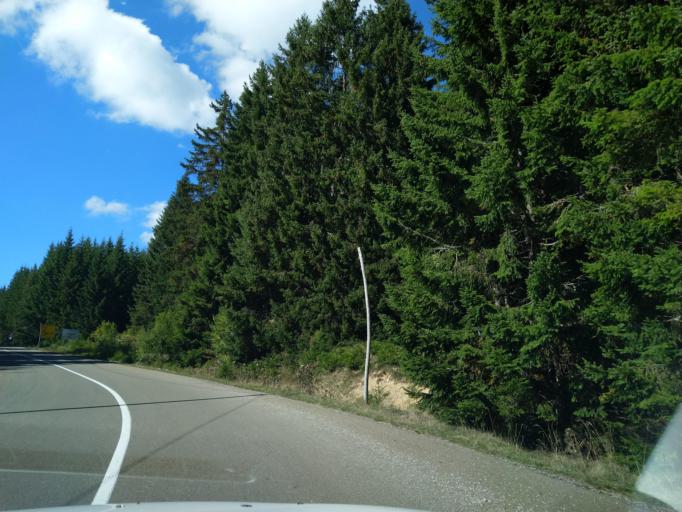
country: RS
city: Sokolovica
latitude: 43.2754
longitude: 20.3481
